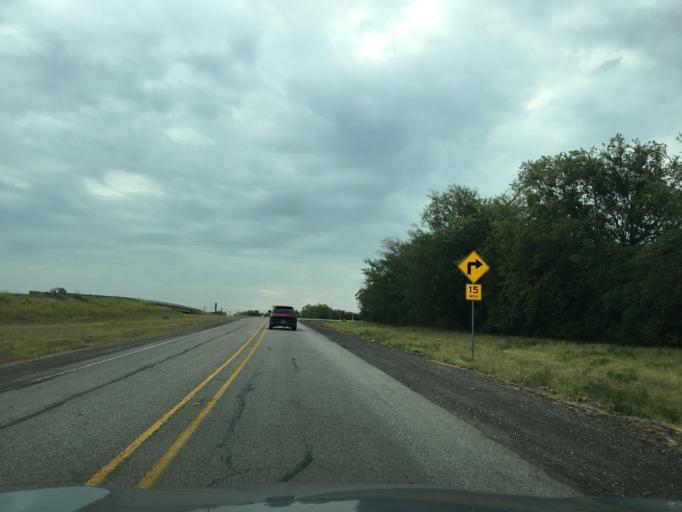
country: US
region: Texas
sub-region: Grayson County
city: Van Alstyne
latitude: 33.3999
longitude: -96.5824
